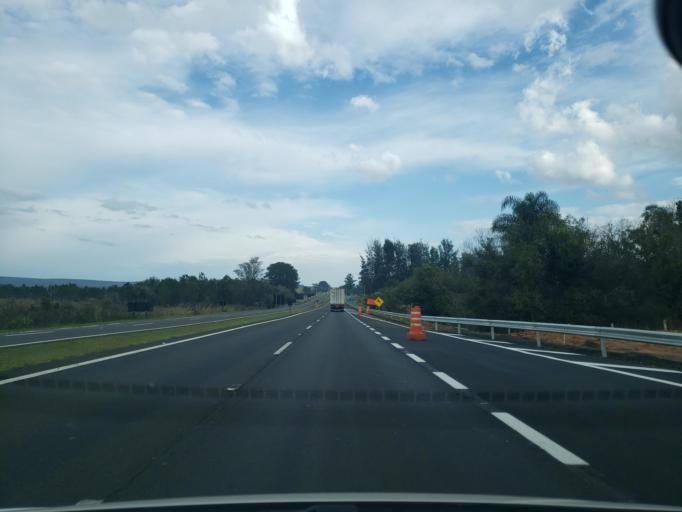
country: BR
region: Sao Paulo
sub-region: Itirapina
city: Itirapina
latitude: -22.2644
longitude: -47.9092
